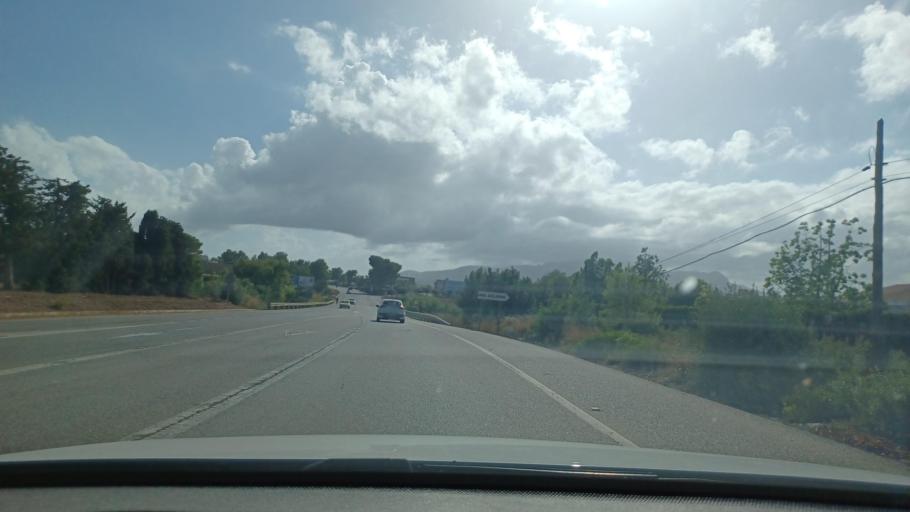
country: ES
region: Catalonia
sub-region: Provincia de Tarragona
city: Vilanova d'Escornalbou
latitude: 41.0262
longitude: 0.9592
